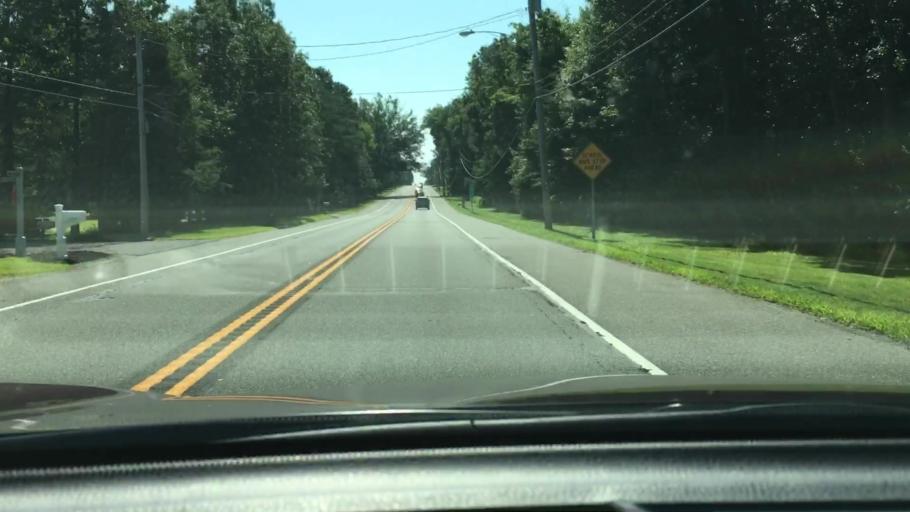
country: US
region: New Jersey
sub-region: Cumberland County
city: Laurel Lake
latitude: 39.3696
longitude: -74.9409
